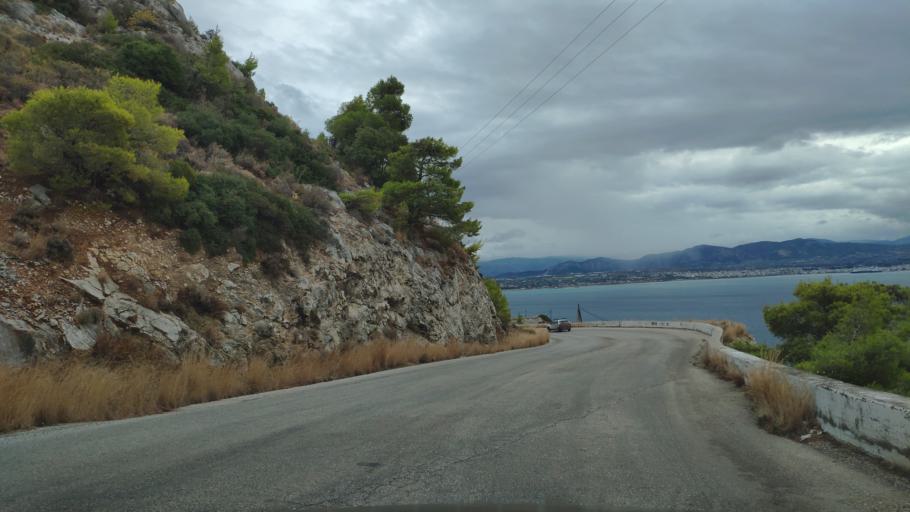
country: GR
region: Peloponnese
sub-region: Nomos Korinthias
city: Perachora
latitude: 37.9977
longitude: 22.9490
